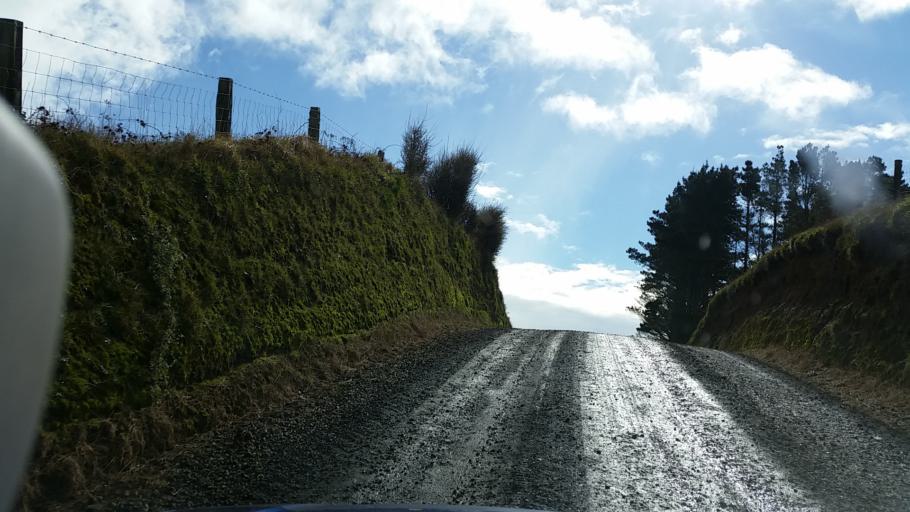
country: NZ
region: Taranaki
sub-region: South Taranaki District
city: Eltham
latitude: -39.2789
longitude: 174.3081
